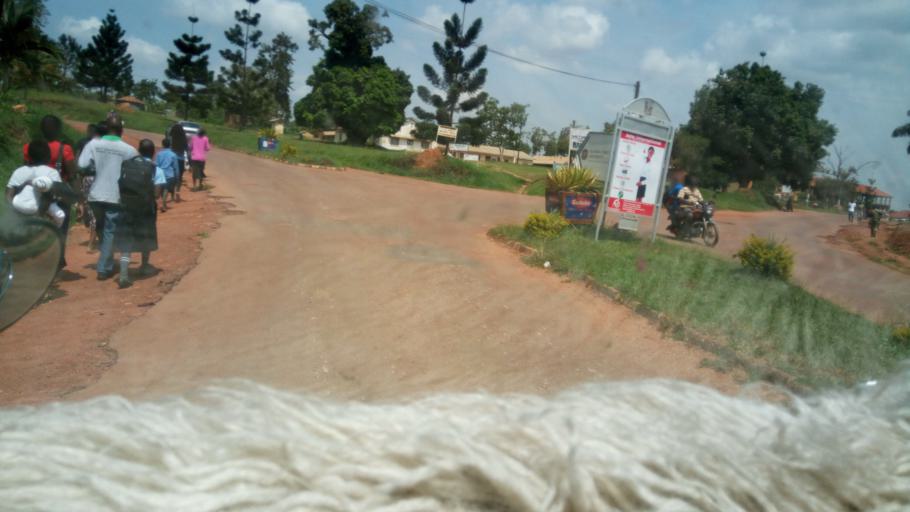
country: UG
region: Central Region
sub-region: Mukono District
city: Mukono
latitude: 0.3609
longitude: 32.7425
